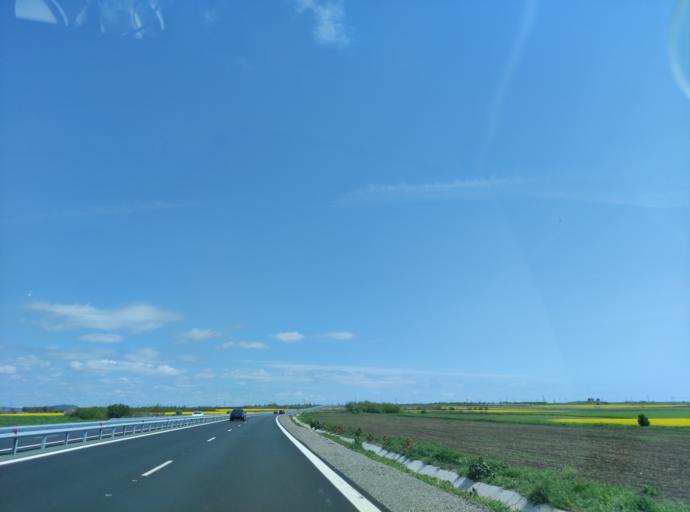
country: BG
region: Burgas
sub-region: Obshtina Pomorie
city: Pomorie
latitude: 42.5720
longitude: 27.5746
